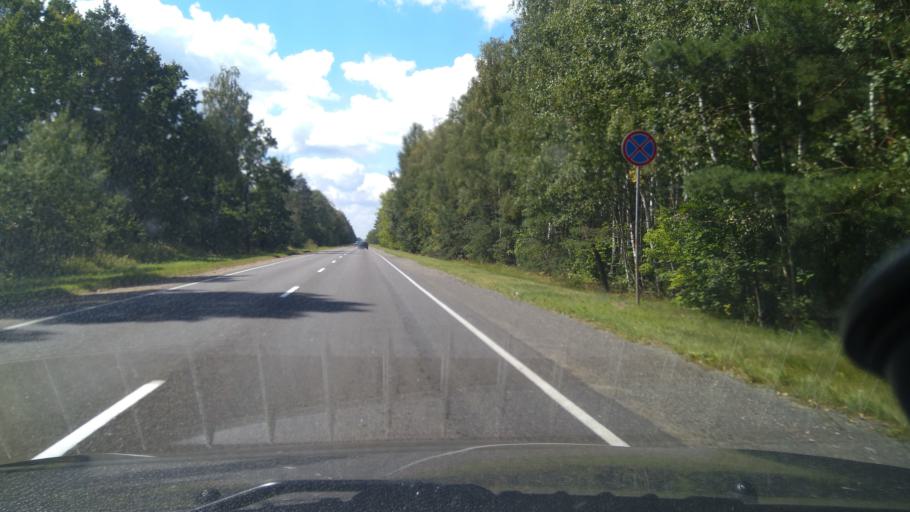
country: BY
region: Brest
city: Nyakhachava
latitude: 52.6628
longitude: 25.2435
